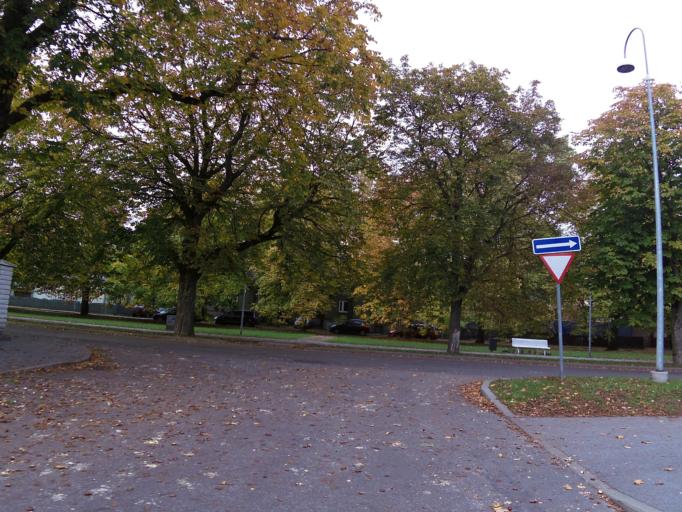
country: EE
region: Harju
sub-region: Tallinna linn
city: Tallinn
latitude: 59.4405
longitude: 24.7126
